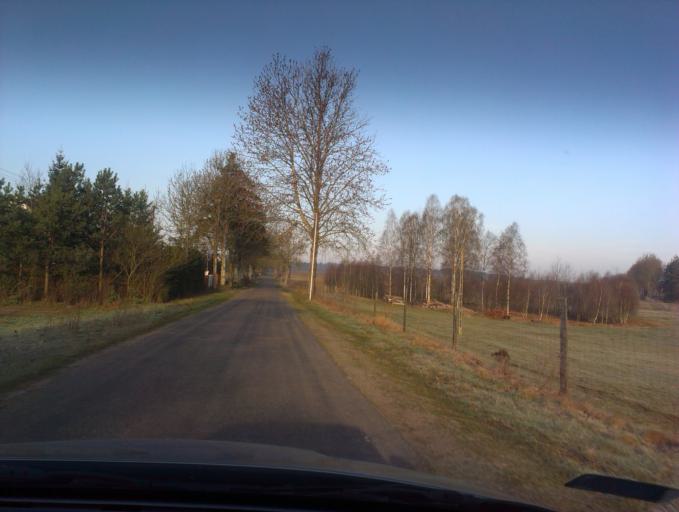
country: PL
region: West Pomeranian Voivodeship
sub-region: Powiat szczecinecki
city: Szczecinek
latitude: 53.8019
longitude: 16.6615
